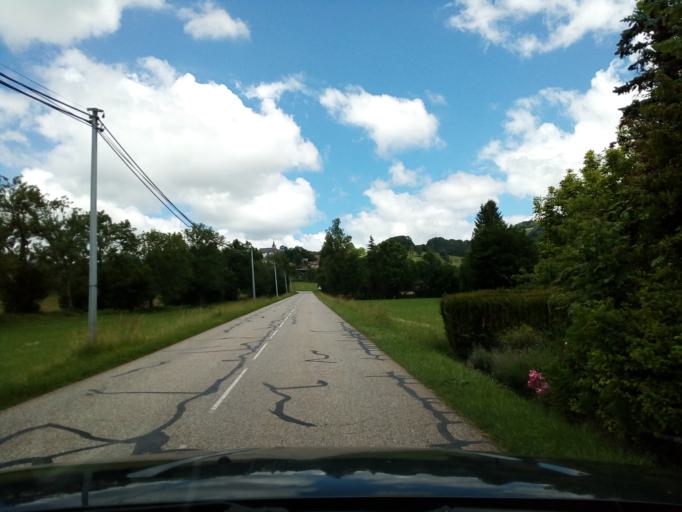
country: FR
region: Rhone-Alpes
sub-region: Departement de la Savoie
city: Les Echelles
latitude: 45.4448
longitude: 5.7534
